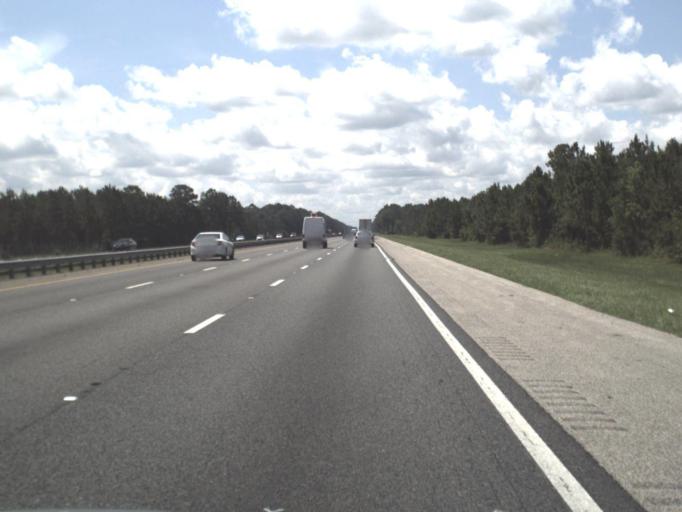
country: US
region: Florida
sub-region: Saint Johns County
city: Saint Augustine Shores
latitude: 29.8030
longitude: -81.3688
